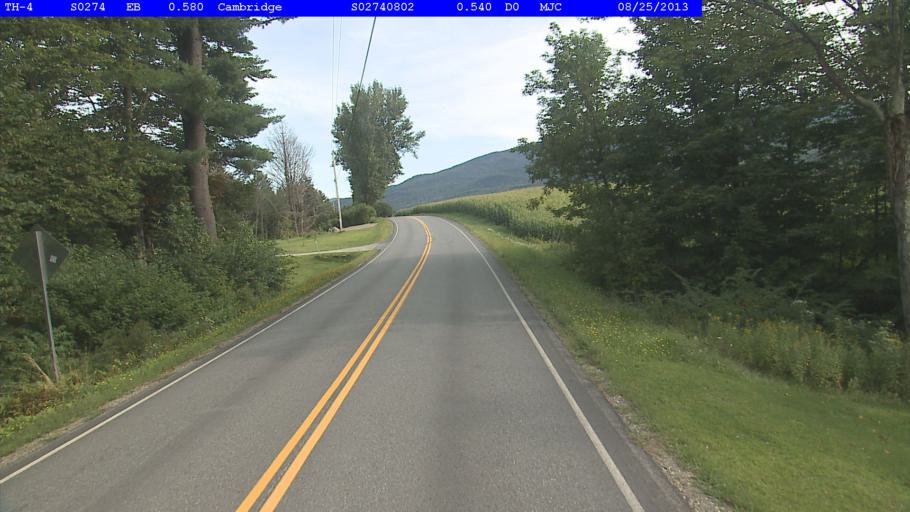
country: US
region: Vermont
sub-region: Lamoille County
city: Johnson
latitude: 44.6753
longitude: -72.7685
